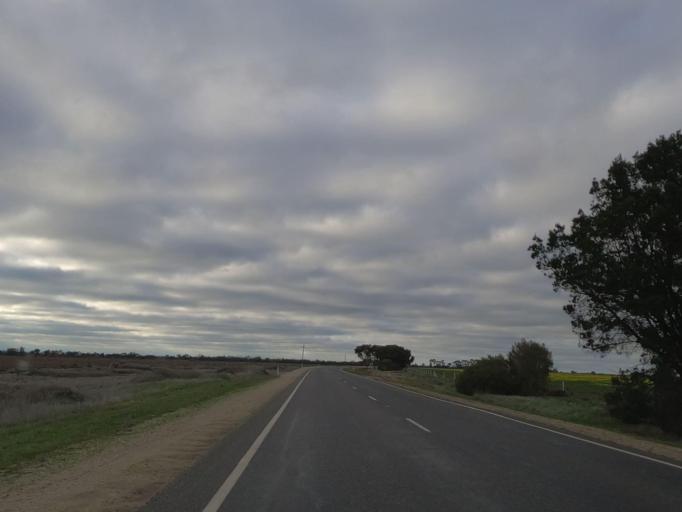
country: AU
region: Victoria
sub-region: Swan Hill
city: Swan Hill
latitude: -35.8298
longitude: 143.9447
